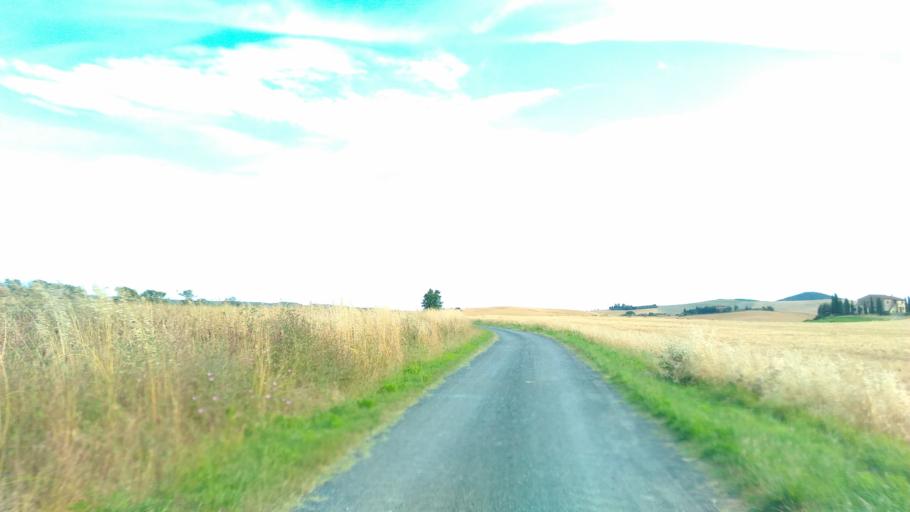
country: IT
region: Tuscany
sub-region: Province of Pisa
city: Santa Luce
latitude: 43.4458
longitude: 10.5208
